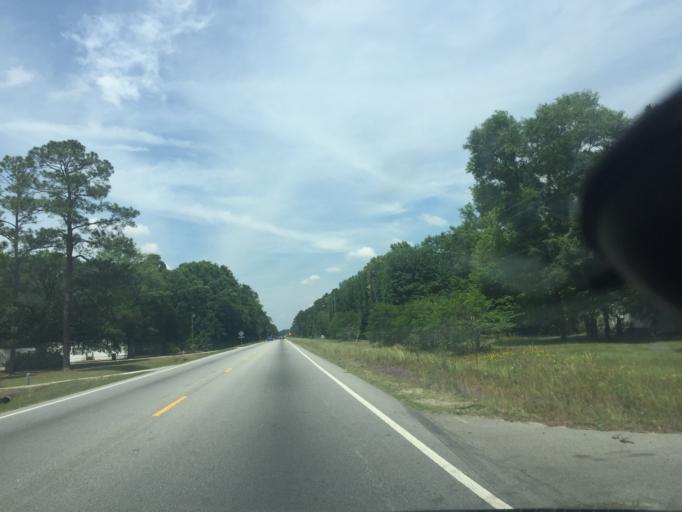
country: US
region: Georgia
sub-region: Chatham County
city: Bloomingdale
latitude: 32.1761
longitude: -81.3927
